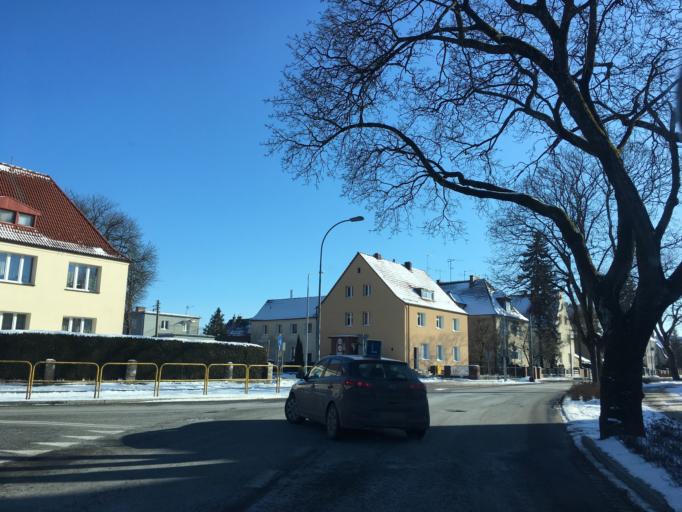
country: PL
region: Pomeranian Voivodeship
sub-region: Slupsk
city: Slupsk
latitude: 54.4594
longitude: 17.0426
